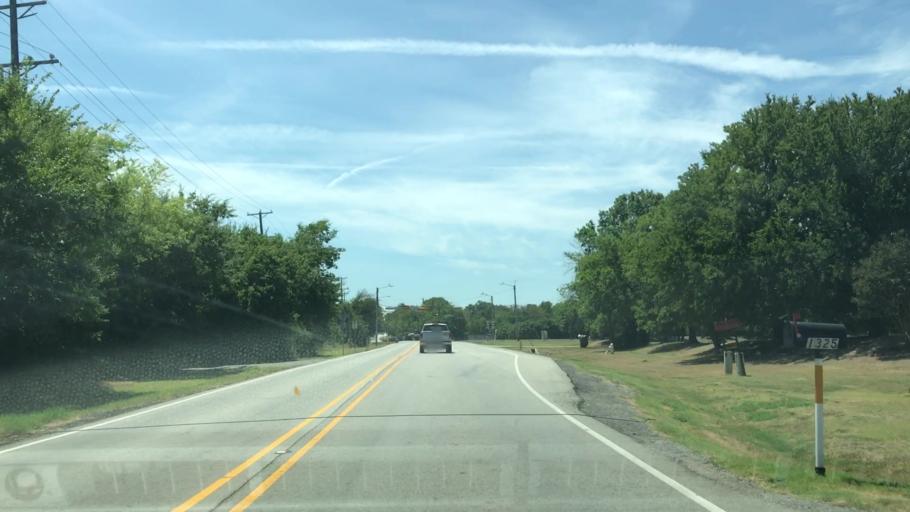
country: US
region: Texas
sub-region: Collin County
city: Lucas
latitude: 33.1026
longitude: -96.5939
